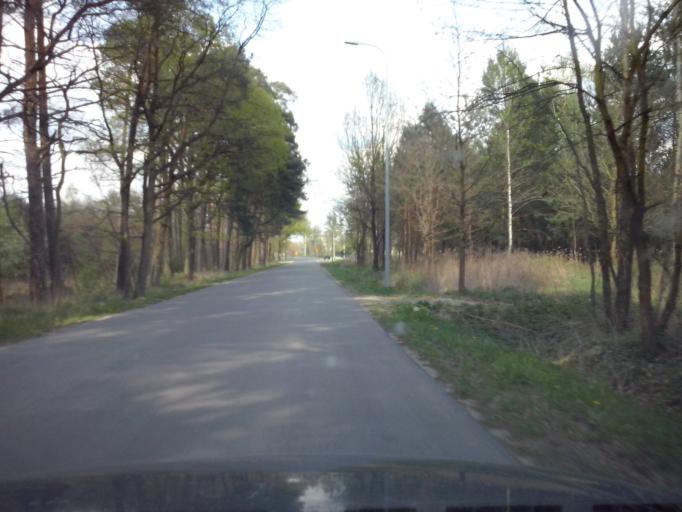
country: PL
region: Subcarpathian Voivodeship
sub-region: Powiat lezajski
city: Letownia
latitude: 50.3616
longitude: 22.2090
